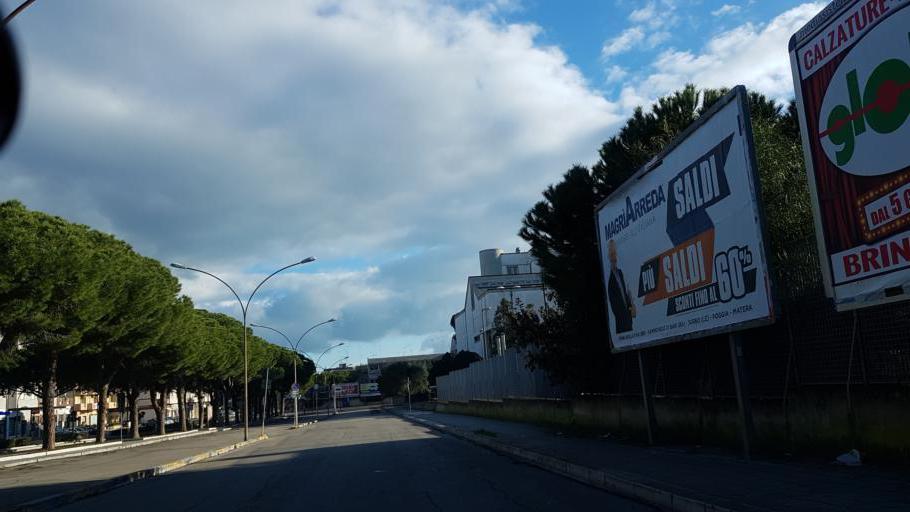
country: IT
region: Apulia
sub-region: Provincia di Brindisi
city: Brindisi
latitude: 40.6234
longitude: 17.9265
